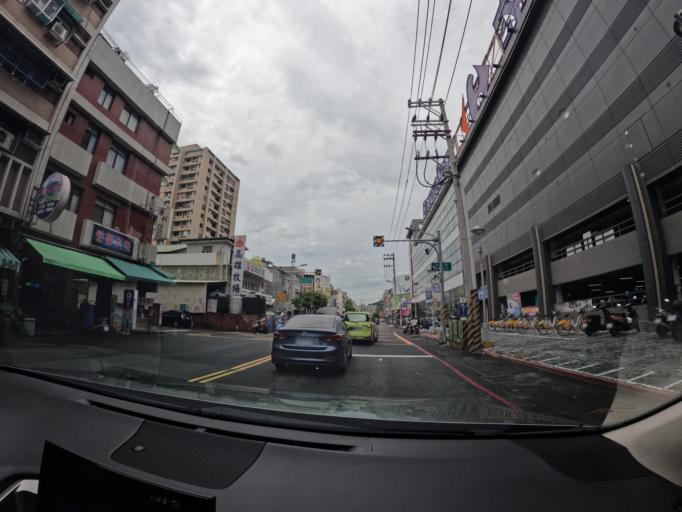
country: TW
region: Kaohsiung
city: Kaohsiung
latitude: 22.6528
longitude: 120.3184
